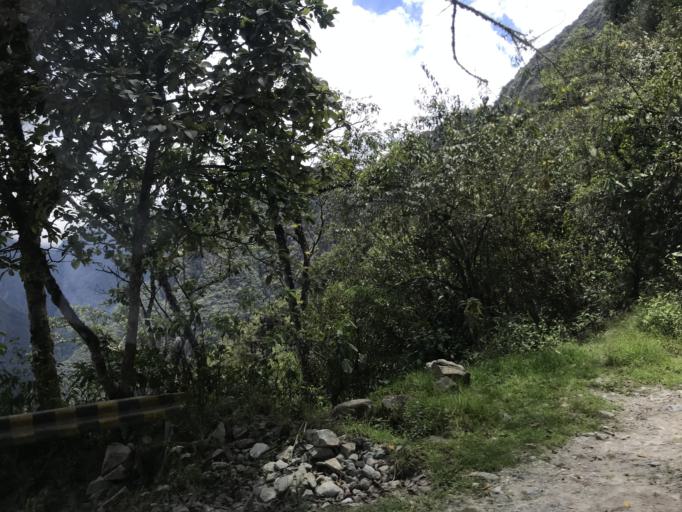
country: PE
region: Cusco
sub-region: Provincia de La Convencion
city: Santa Teresa
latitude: -13.1679
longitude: -72.5389
